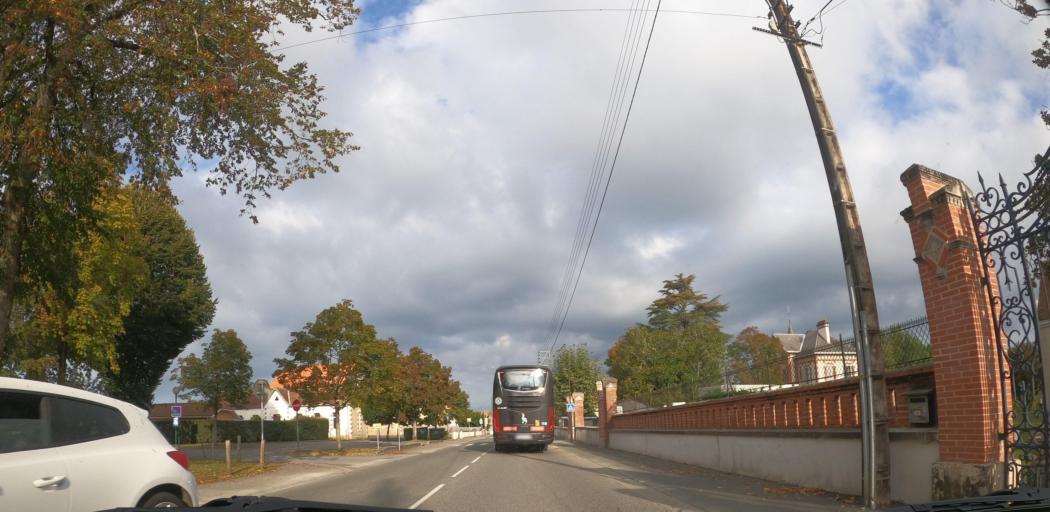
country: FR
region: Aquitaine
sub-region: Departement des Landes
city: Soustons
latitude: 43.7519
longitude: -1.3235
